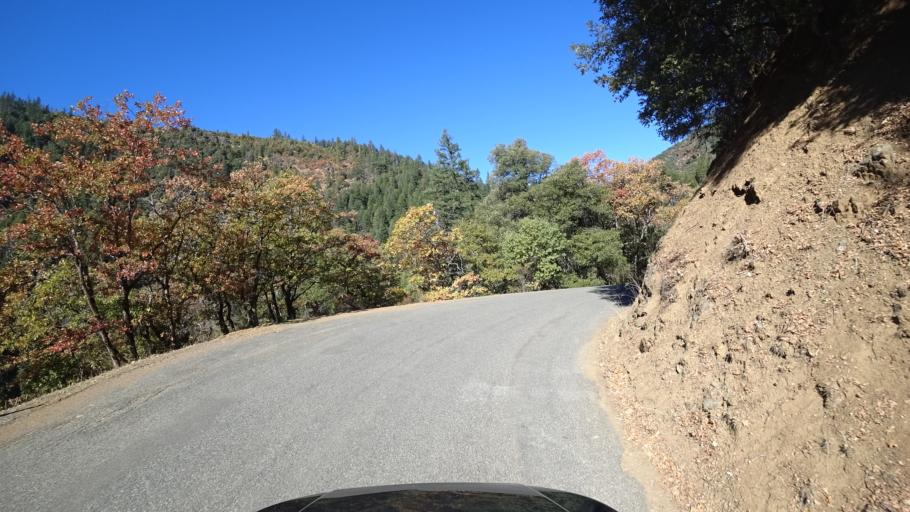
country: US
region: California
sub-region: Humboldt County
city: Willow Creek
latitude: 41.2264
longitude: -123.2563
